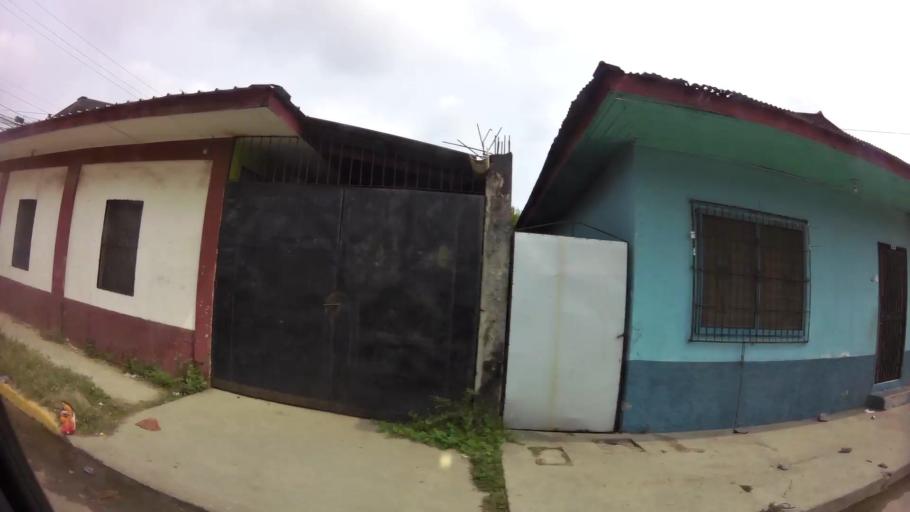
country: HN
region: Atlantida
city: Tela
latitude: 15.7803
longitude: -87.4519
